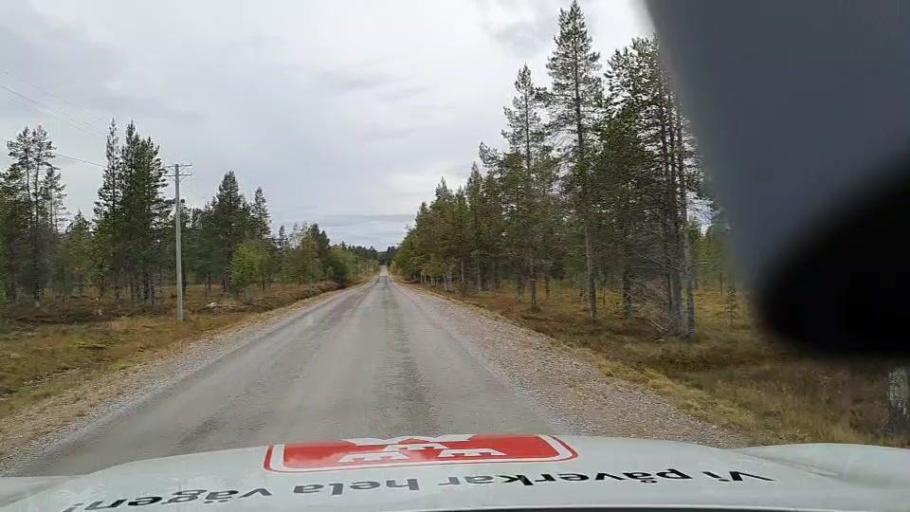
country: NO
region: Hedmark
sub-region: Engerdal
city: Engerdal
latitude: 62.0929
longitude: 12.7975
